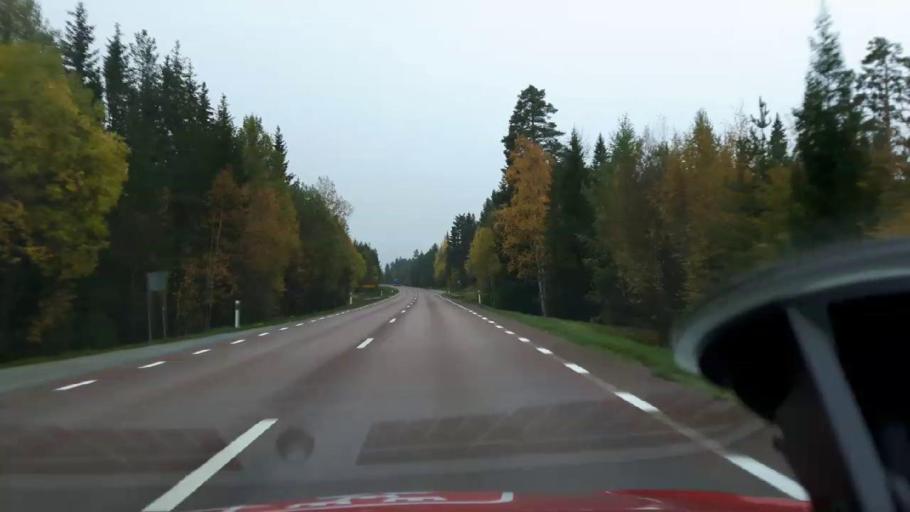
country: SE
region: Jaemtland
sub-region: Bergs Kommun
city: Hoverberg
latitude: 62.6089
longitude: 14.4016
